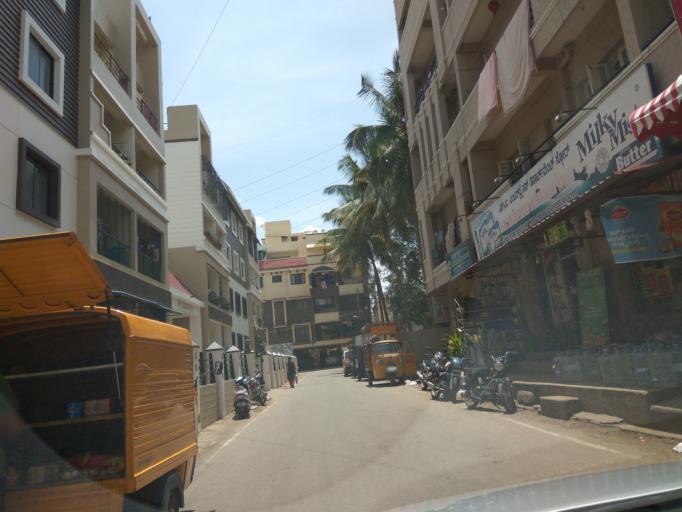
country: IN
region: Karnataka
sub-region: Bangalore Urban
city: Bangalore
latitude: 12.9813
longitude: 77.6759
